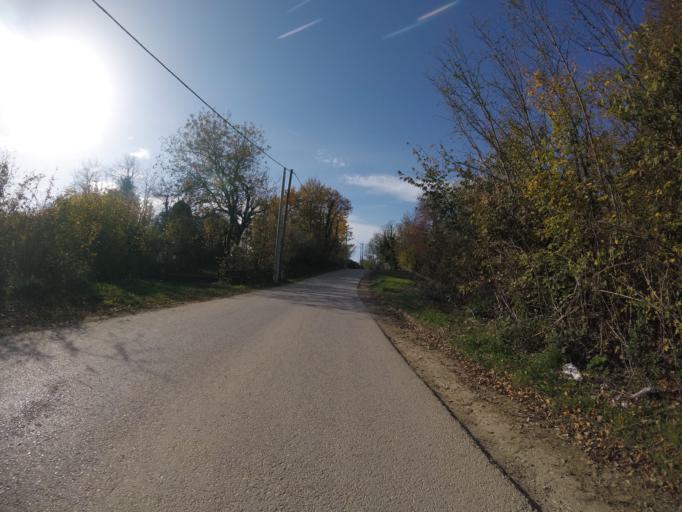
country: HR
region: Zagrebacka
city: Lukavec
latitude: 45.6161
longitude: 16.0126
